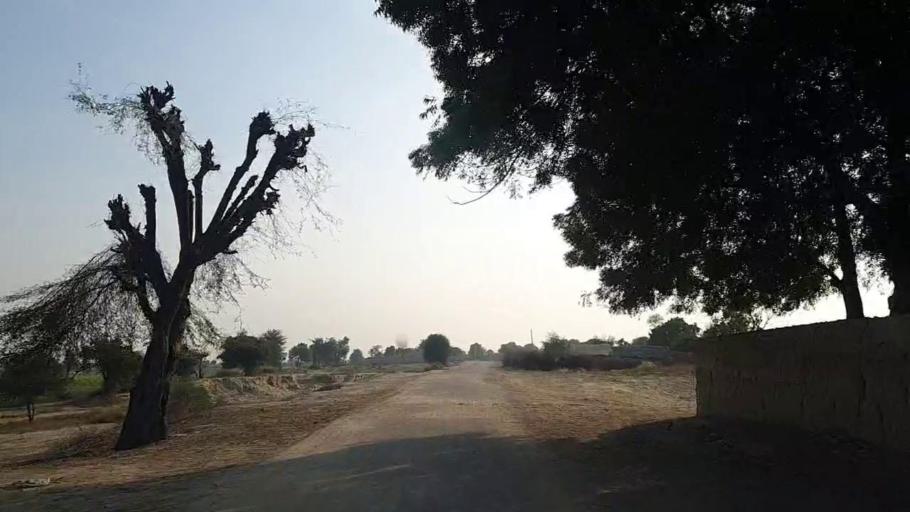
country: PK
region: Sindh
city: Jam Sahib
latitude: 26.4488
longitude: 68.5838
